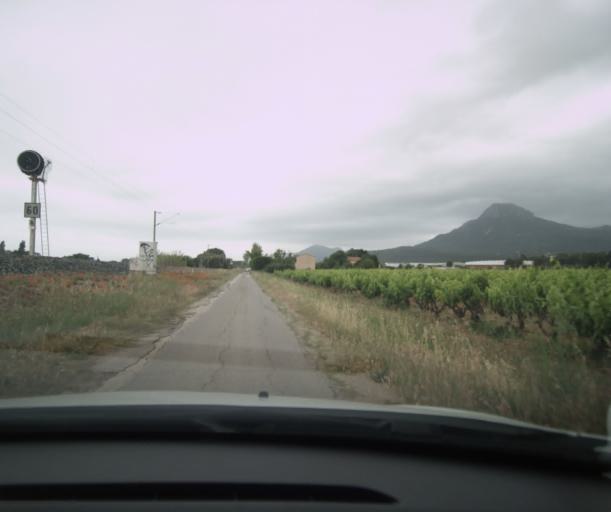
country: FR
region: Provence-Alpes-Cote d'Azur
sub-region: Departement du Var
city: La Crau
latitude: 43.1446
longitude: 6.0504
